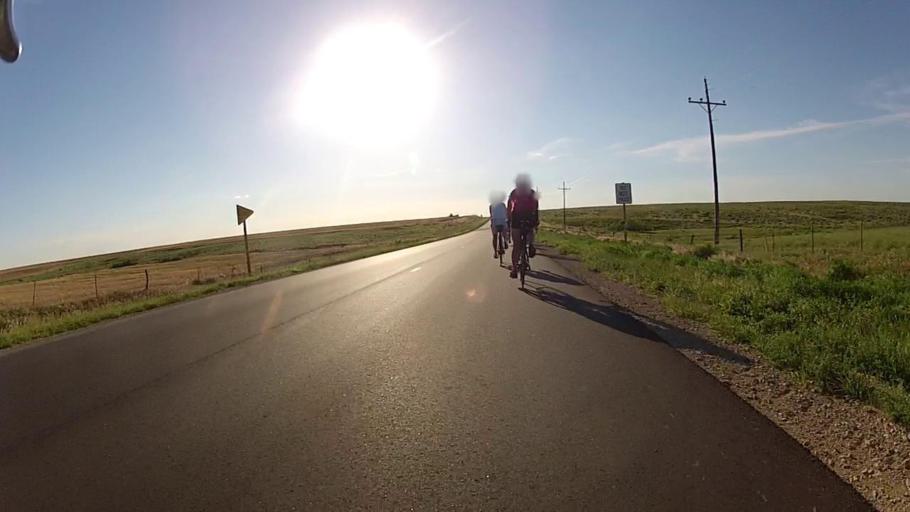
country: US
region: Kansas
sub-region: Comanche County
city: Coldwater
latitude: 37.2821
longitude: -99.1075
